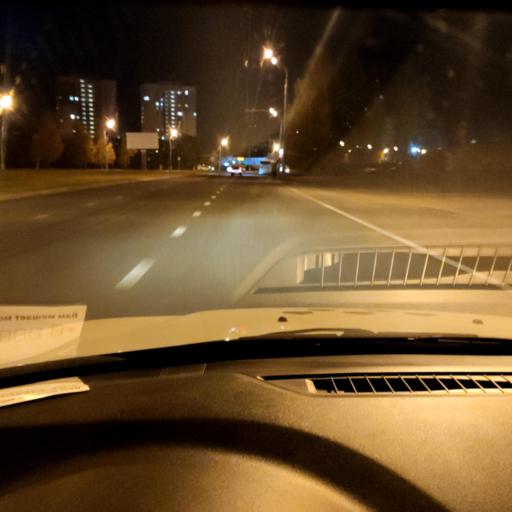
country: RU
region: Samara
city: Tol'yatti
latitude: 53.5041
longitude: 49.2579
